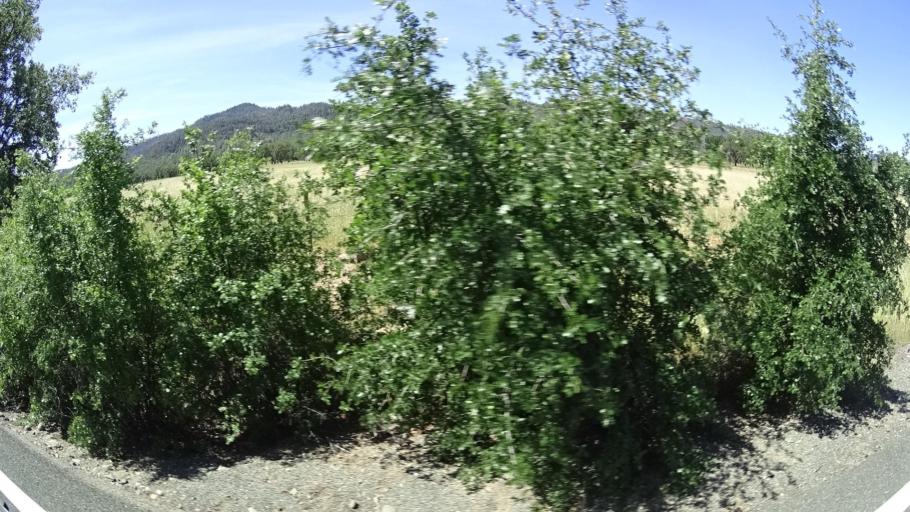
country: US
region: California
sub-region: Lake County
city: Middletown
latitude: 38.7380
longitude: -122.5666
